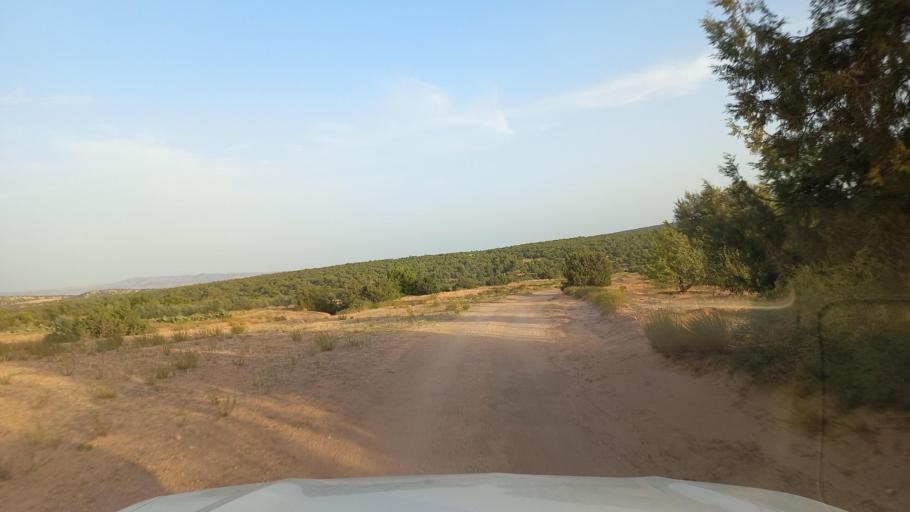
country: TN
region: Al Qasrayn
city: Sbiba
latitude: 35.4119
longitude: 8.9123
